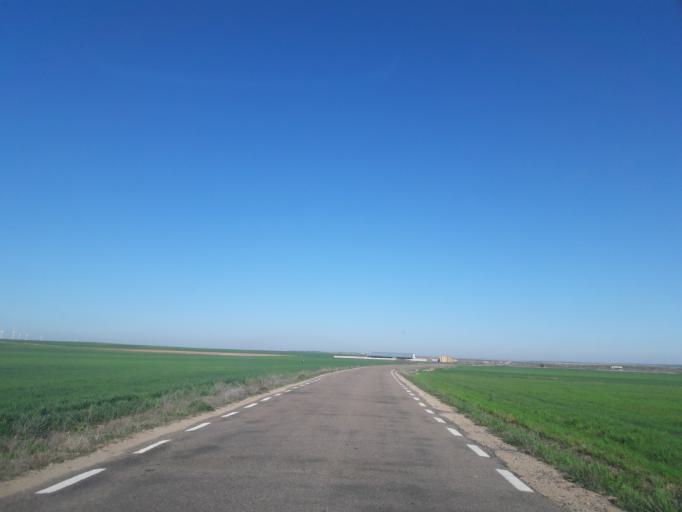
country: ES
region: Castille and Leon
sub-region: Provincia de Salamanca
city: Coca de Alba
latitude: 40.8635
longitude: -5.3694
